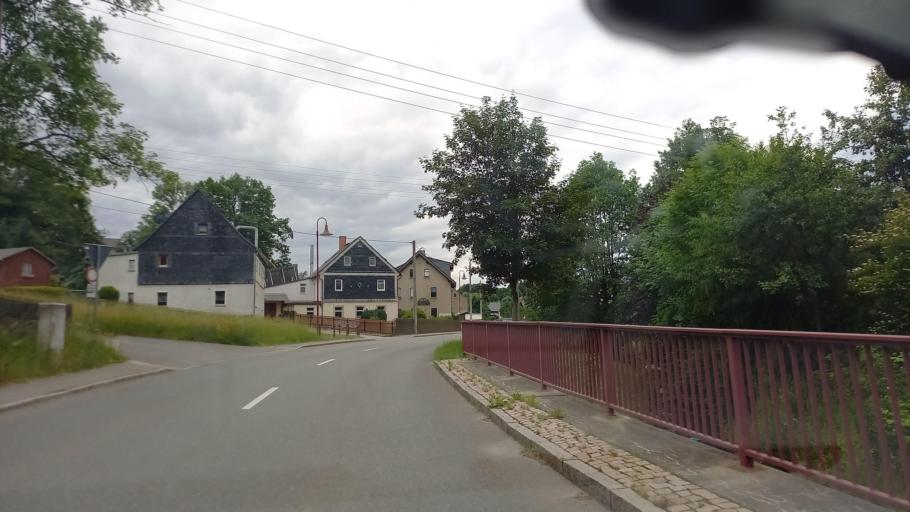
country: DE
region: Saxony
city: Kirchberg
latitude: 50.5859
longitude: 12.5441
